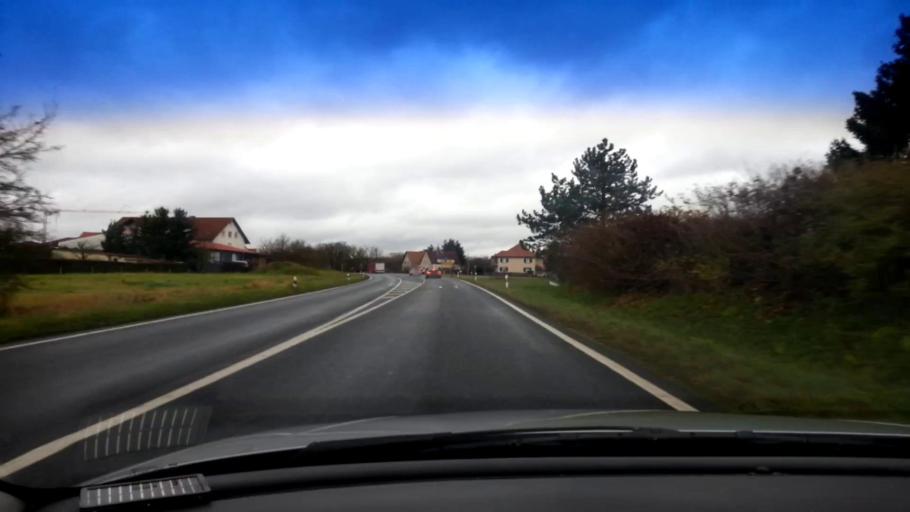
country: DE
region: Bavaria
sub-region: Upper Franconia
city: Rattelsdorf
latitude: 50.0121
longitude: 10.8913
